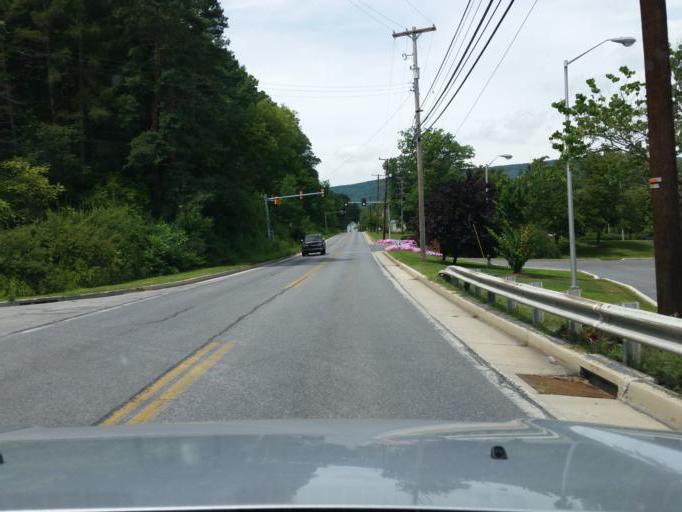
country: US
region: Pennsylvania
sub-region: Blair County
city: Altoona
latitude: 40.5384
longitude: -78.4092
